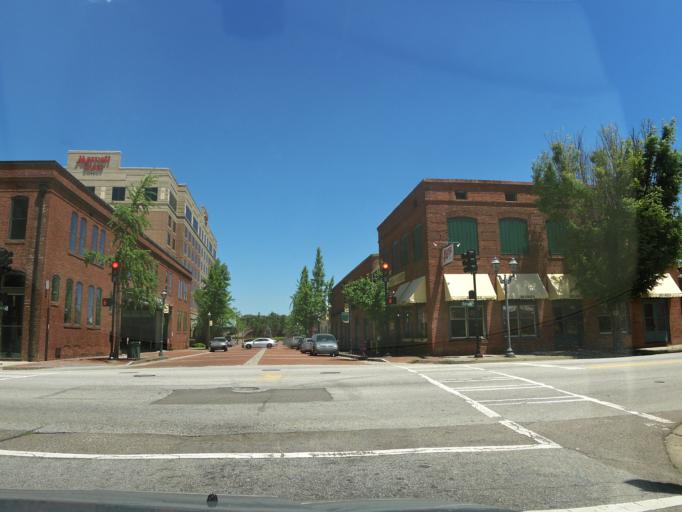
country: US
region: Georgia
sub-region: Richmond County
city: Augusta
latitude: 33.4773
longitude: -81.9668
